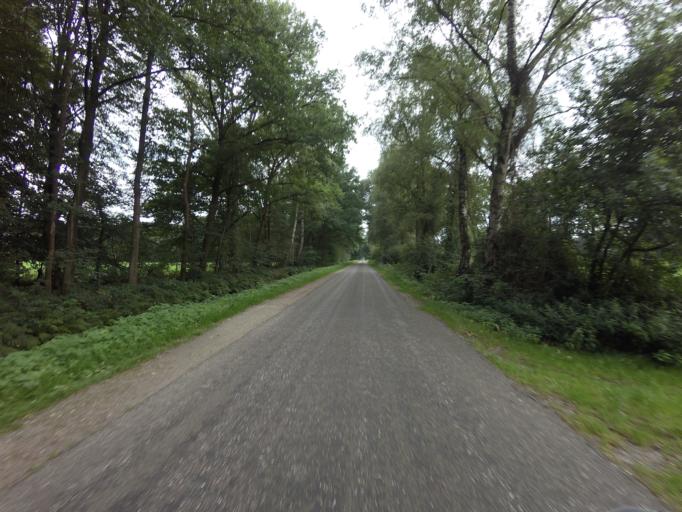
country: DE
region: Lower Saxony
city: Lage
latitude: 52.4666
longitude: 6.9499
